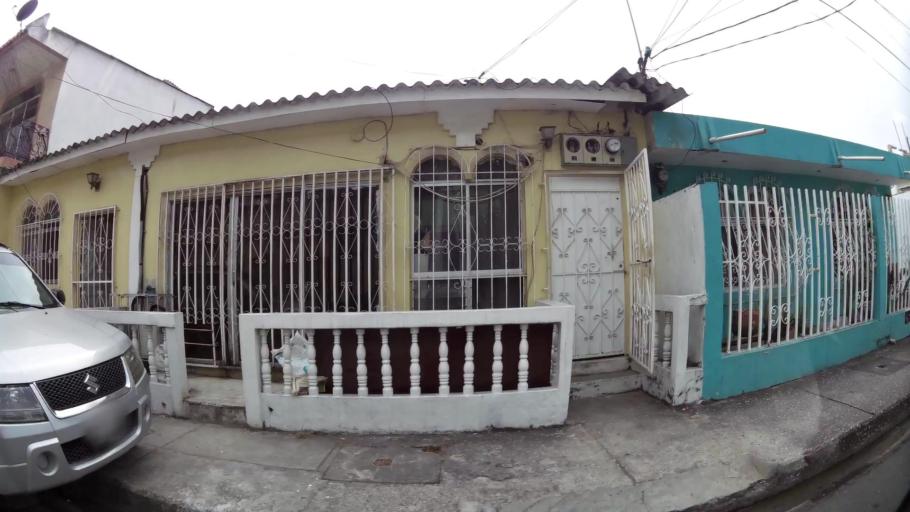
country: EC
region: Guayas
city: Eloy Alfaro
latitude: -2.1391
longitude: -79.8967
